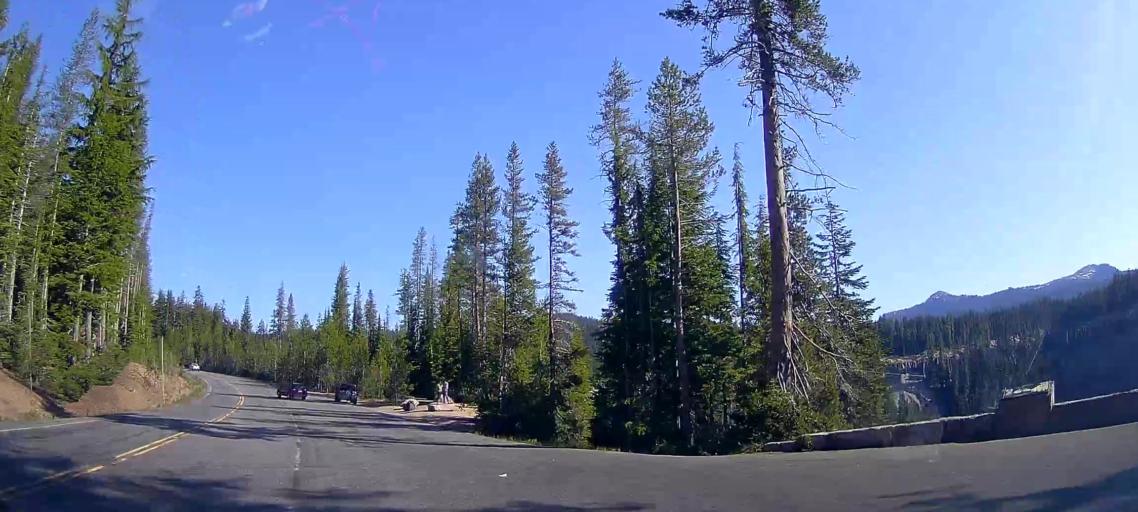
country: US
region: Oregon
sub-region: Jackson County
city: Shady Cove
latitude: 42.8580
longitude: -122.1539
